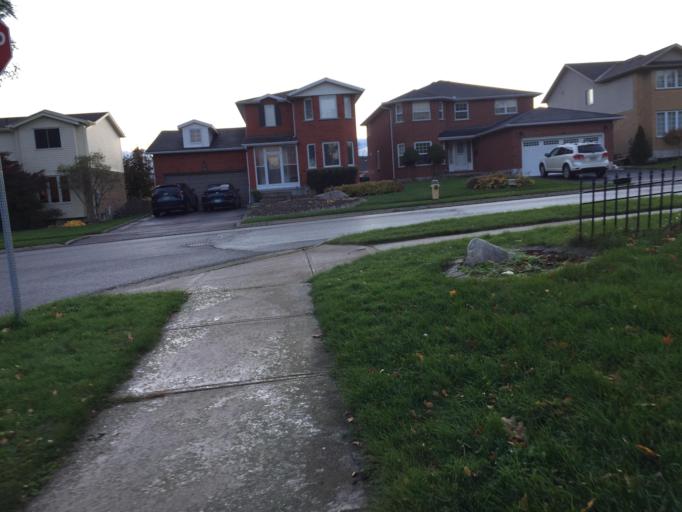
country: CA
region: Ontario
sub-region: Wellington County
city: Guelph
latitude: 43.5300
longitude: -80.2984
